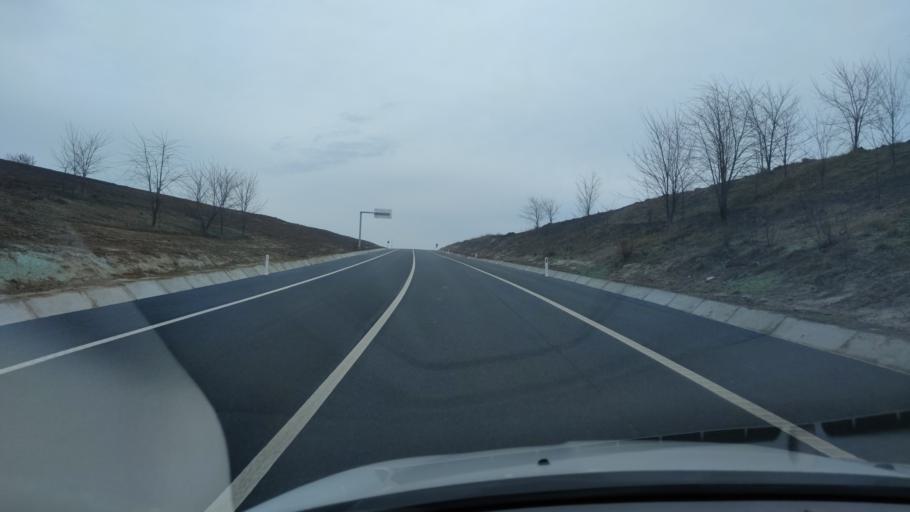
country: RO
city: Szekelyhid
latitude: 47.3282
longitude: 22.0843
